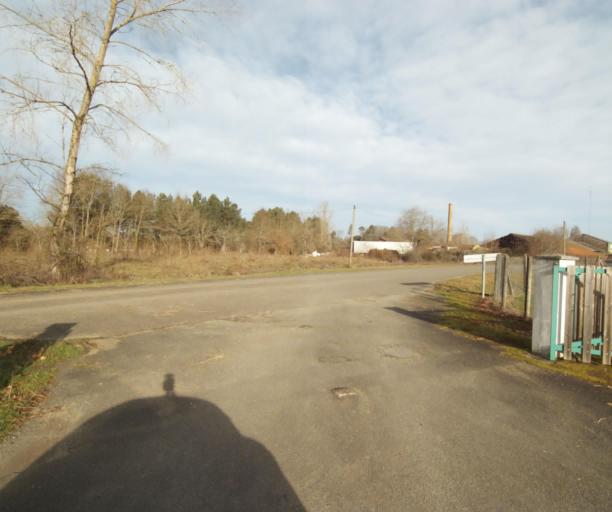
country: FR
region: Aquitaine
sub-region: Departement des Landes
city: Gabarret
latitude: 43.9830
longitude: 0.0209
